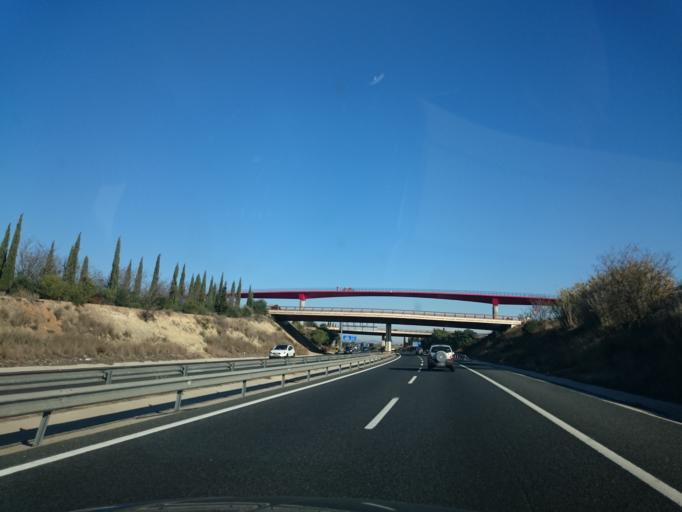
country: ES
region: Catalonia
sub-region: Provincia de Tarragona
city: Vila-seca
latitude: 41.1039
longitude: 1.1546
